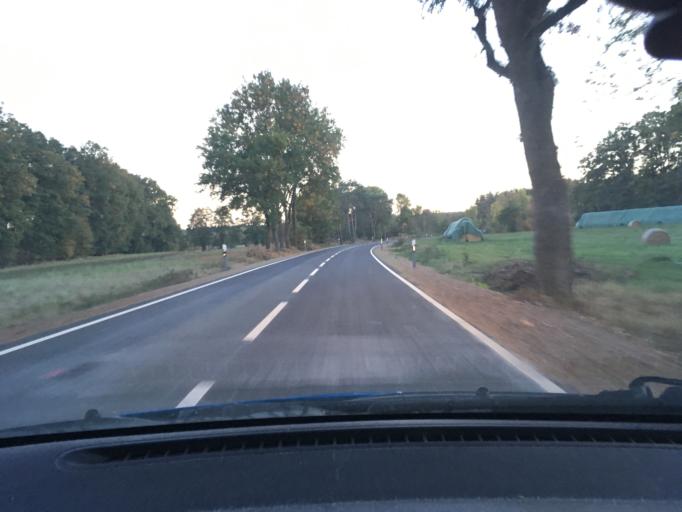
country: DE
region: Lower Saxony
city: Neetze
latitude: 53.2608
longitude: 10.6142
